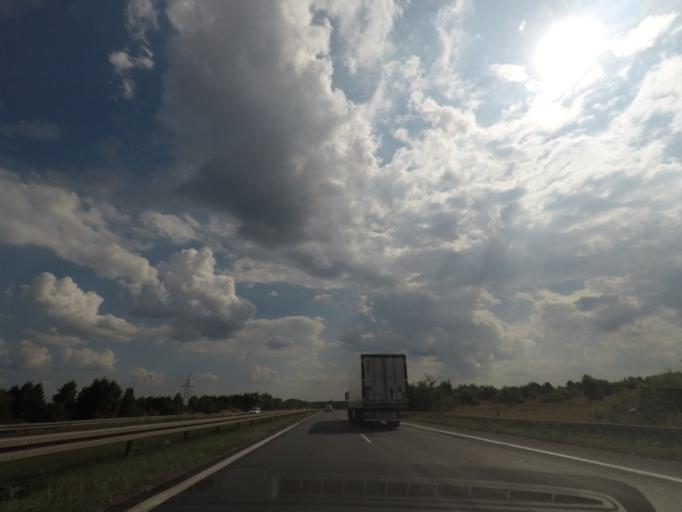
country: PL
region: Lodz Voivodeship
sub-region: Powiat radomszczanski
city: Gomunice
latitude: 51.1849
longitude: 19.4707
